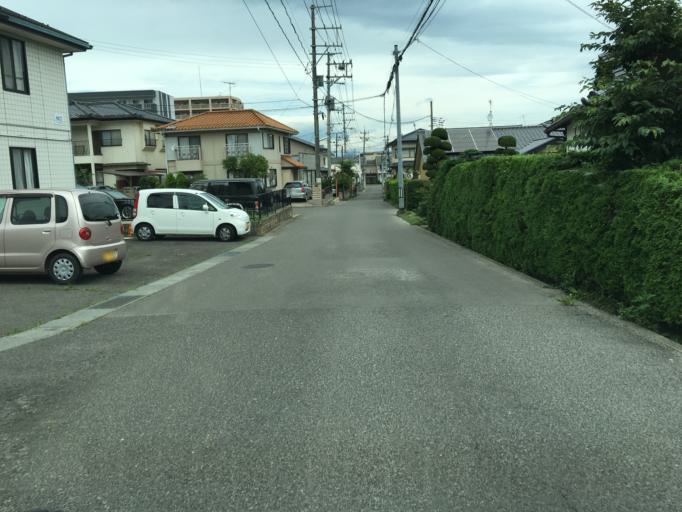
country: JP
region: Fukushima
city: Fukushima-shi
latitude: 37.7280
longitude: 140.4415
